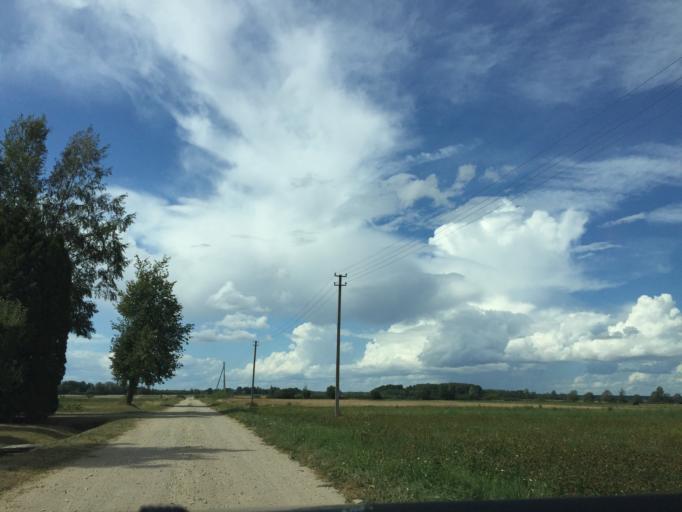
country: LT
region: Siauliu apskritis
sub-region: Joniskis
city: Joniskis
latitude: 56.3146
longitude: 23.6354
